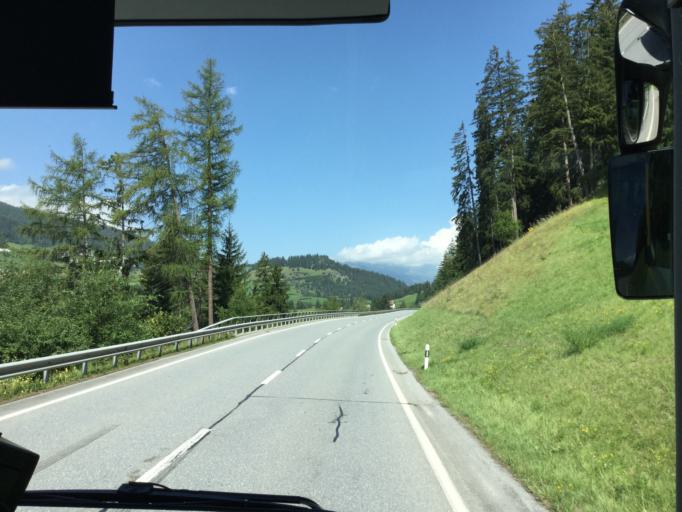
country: CH
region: Grisons
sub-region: Albula District
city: Tiefencastel
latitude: 46.6192
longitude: 9.5911
